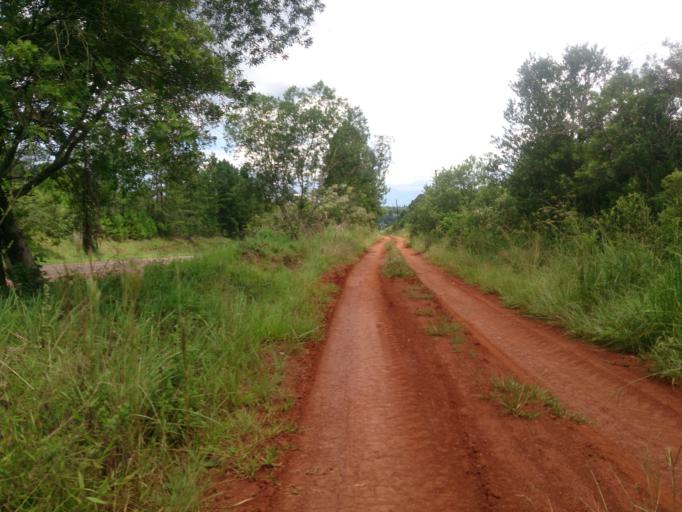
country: AR
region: Misiones
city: Campo Viera
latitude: -27.3616
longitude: -55.0500
